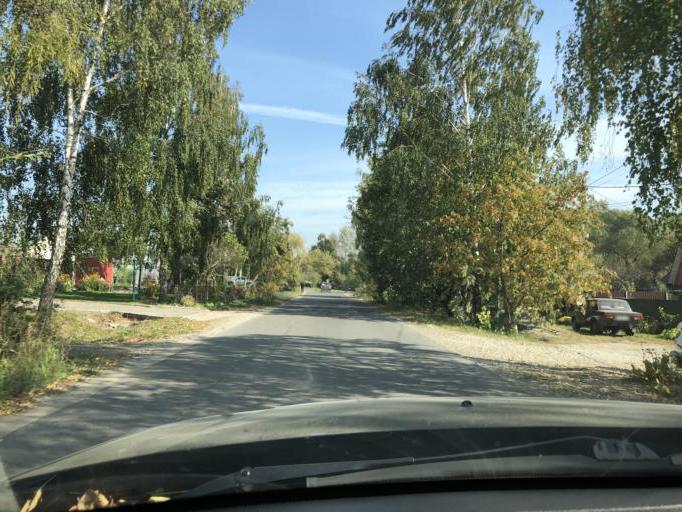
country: RU
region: Tula
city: Yasnogorsk
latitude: 54.4849
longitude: 37.6932
